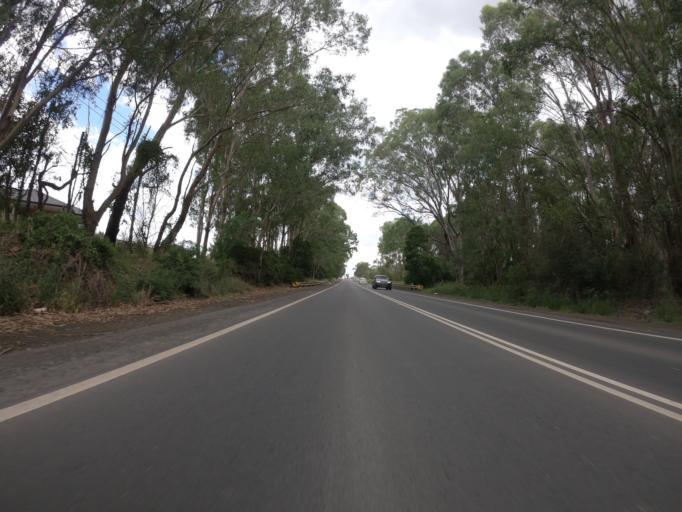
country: AU
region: New South Wales
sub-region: Blacktown
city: Mount Druitt
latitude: -33.8075
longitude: 150.7723
